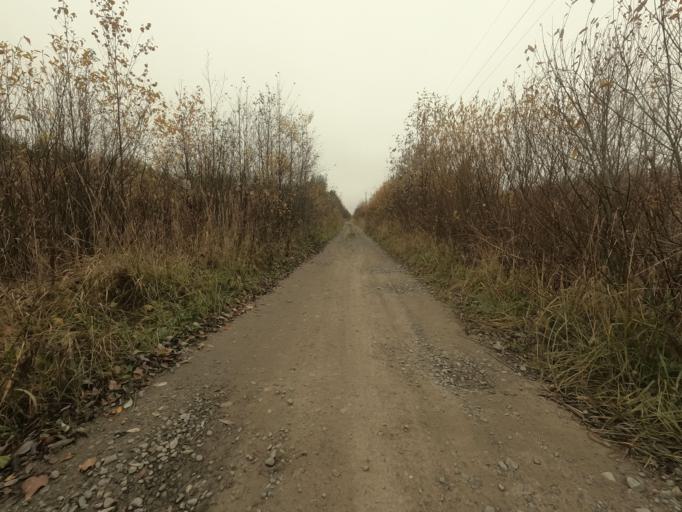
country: RU
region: Leningrad
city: Pavlovo
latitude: 59.7673
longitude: 30.9415
